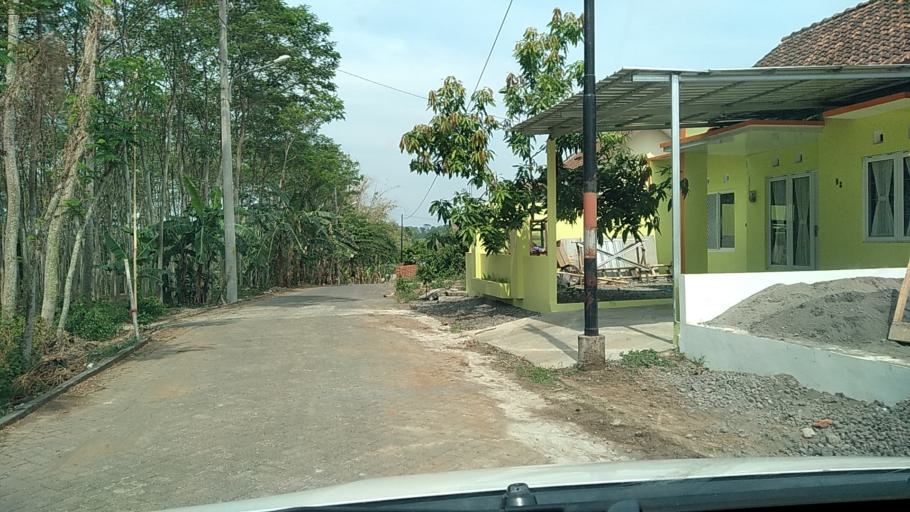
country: ID
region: Central Java
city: Ungaran
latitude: -7.0851
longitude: 110.3167
